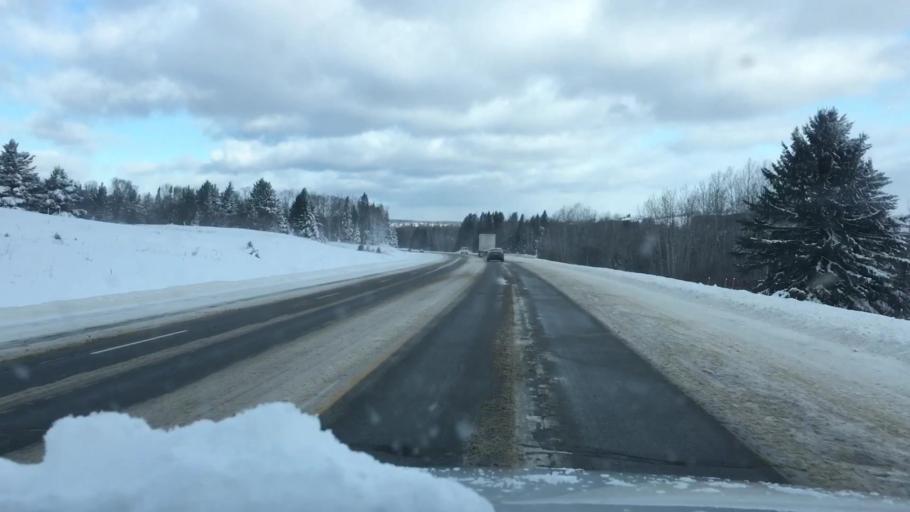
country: US
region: Maine
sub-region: Aroostook County
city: Caribou
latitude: 46.8254
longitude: -67.9936
